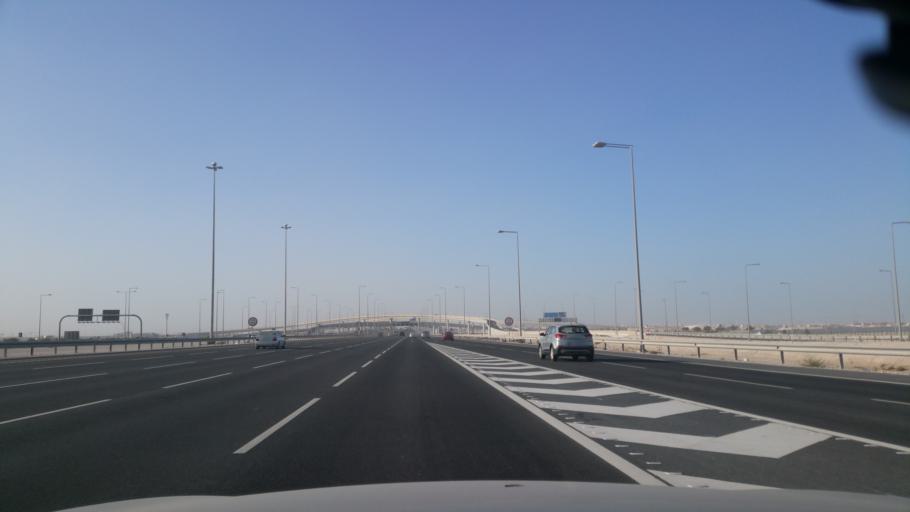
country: QA
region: Al Wakrah
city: Al Wukayr
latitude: 25.1931
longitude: 51.5453
